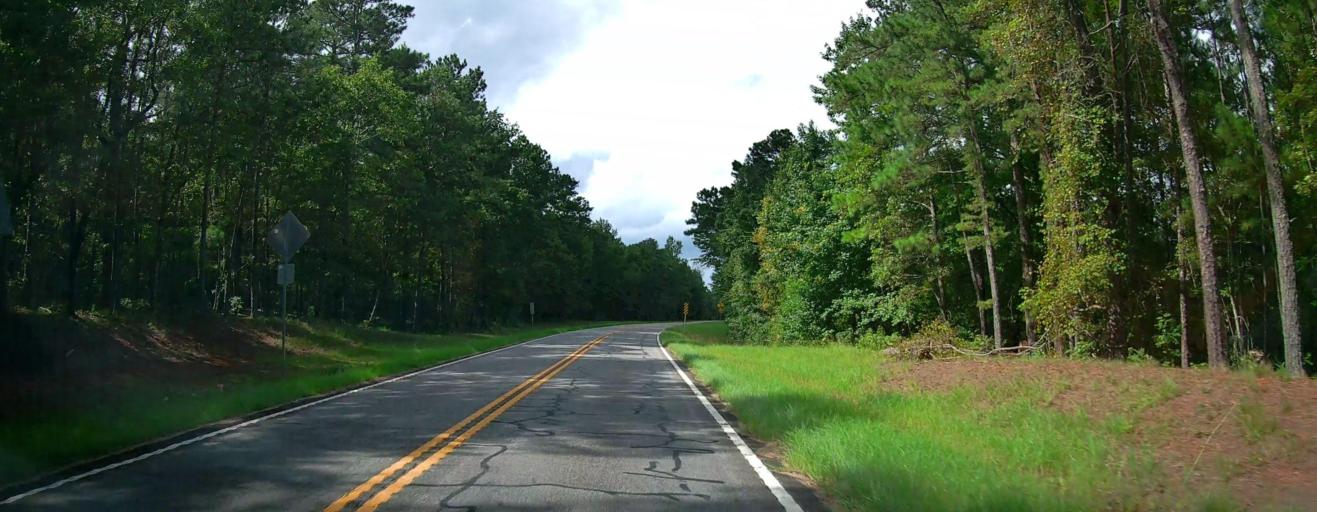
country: US
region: Georgia
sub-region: Talbot County
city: Sardis
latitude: 32.8511
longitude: -84.7076
